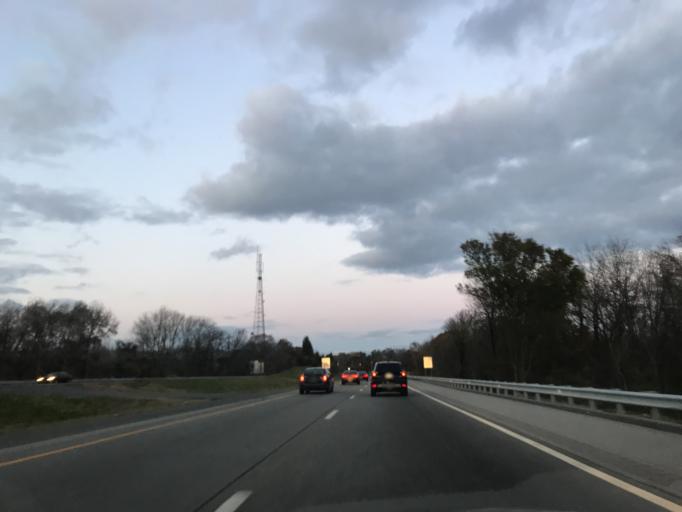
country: US
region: Delaware
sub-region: New Castle County
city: Bellefonte
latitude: 39.7715
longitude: -75.5323
